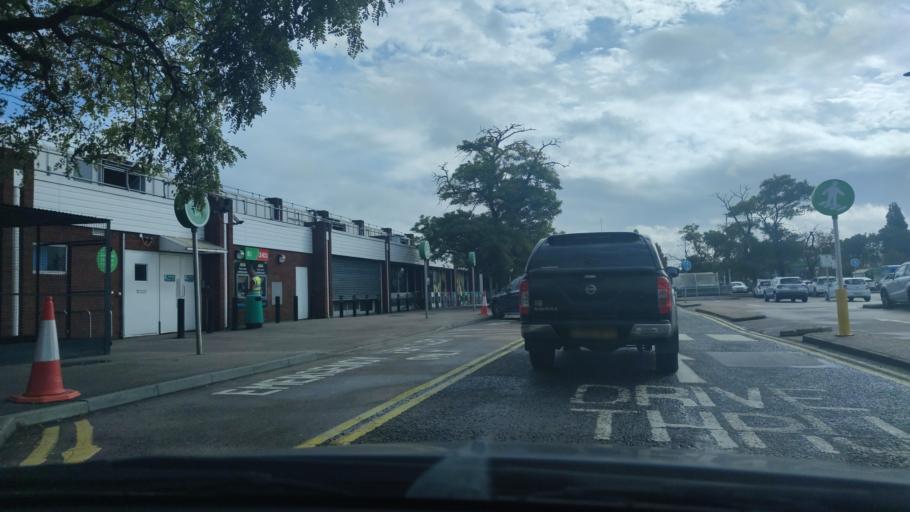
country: GB
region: England
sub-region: Borough of Thurrock
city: Tilbury
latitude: 51.4698
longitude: 0.3449
